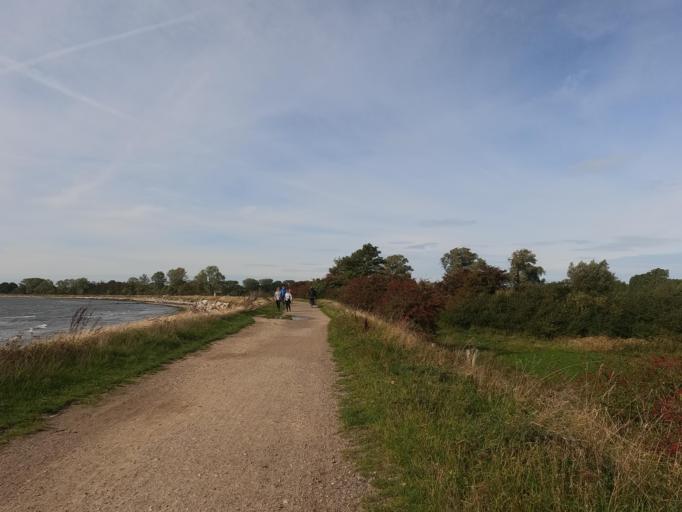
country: DE
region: Schleswig-Holstein
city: Dahme
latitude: 54.1975
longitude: 11.0890
